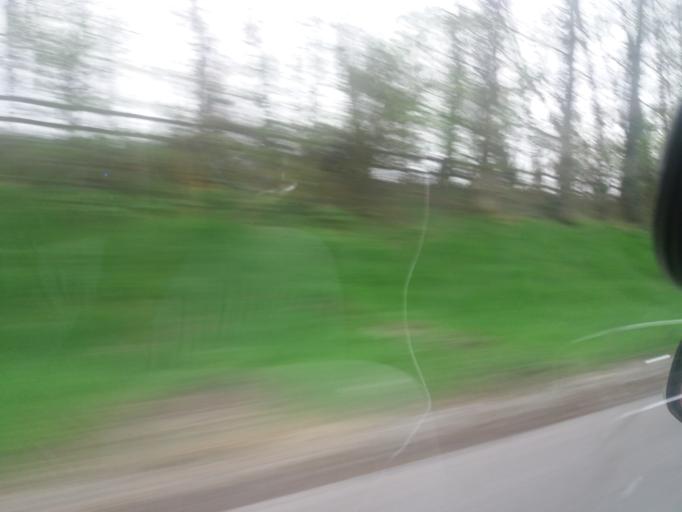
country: IE
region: Munster
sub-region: County Limerick
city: Rathkeale
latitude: 52.5100
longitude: -8.9876
